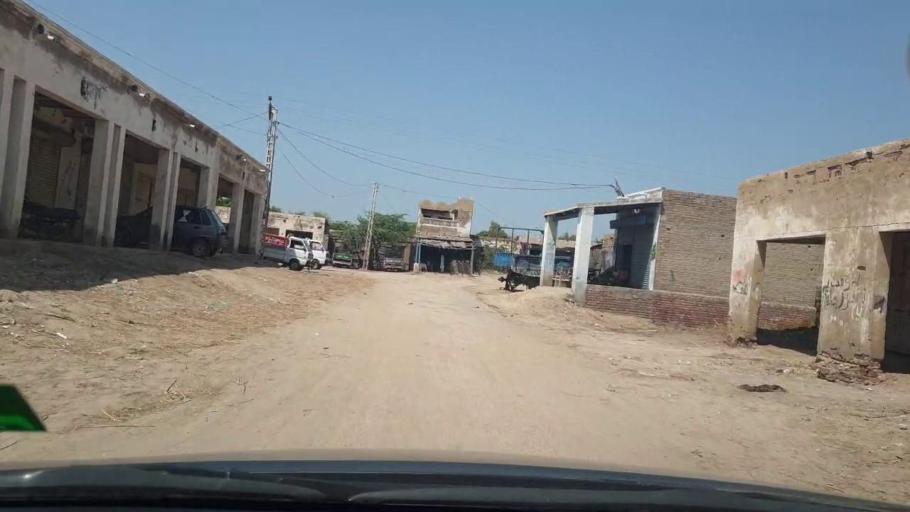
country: PK
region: Sindh
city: Tando Bago
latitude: 24.9264
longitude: 69.0552
